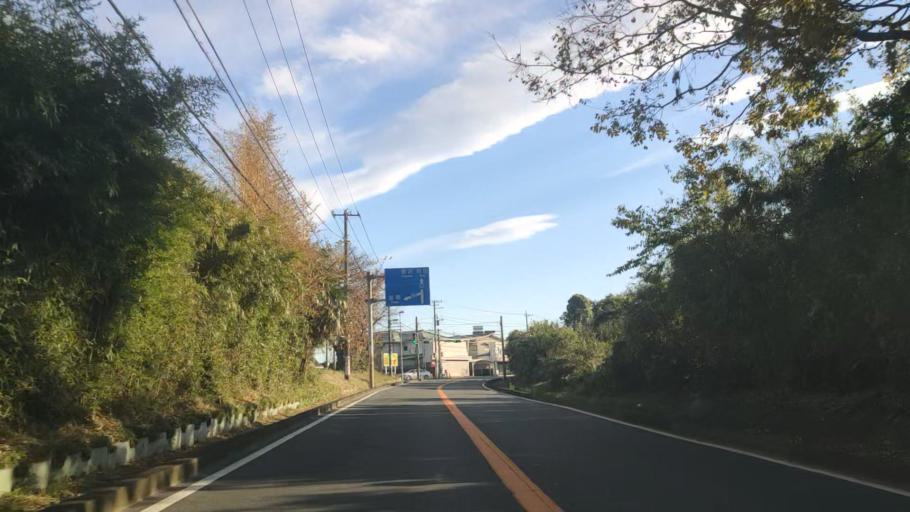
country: JP
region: Kanagawa
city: Atsugi
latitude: 35.4122
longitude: 139.4055
